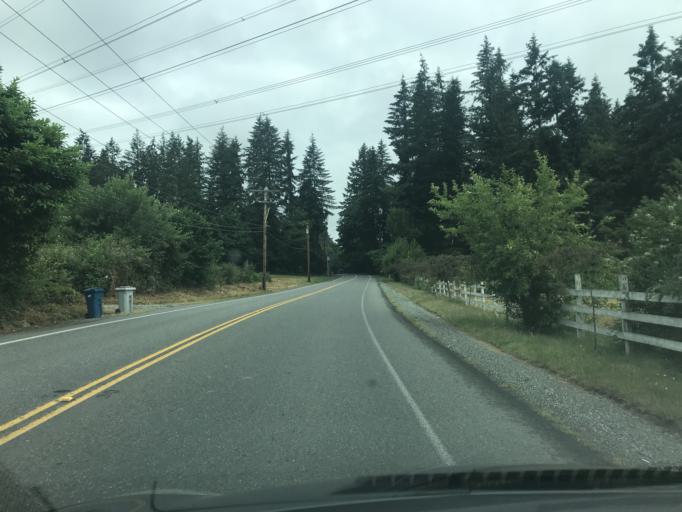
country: US
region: Washington
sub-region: King County
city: Lake Morton-Berrydale
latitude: 47.3456
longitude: -122.1058
